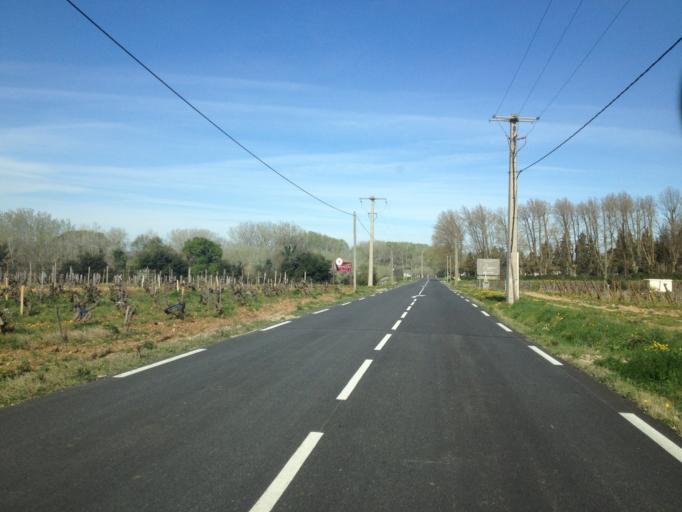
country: FR
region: Languedoc-Roussillon
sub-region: Departement du Gard
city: Roquemaure
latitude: 44.0608
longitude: 4.7999
